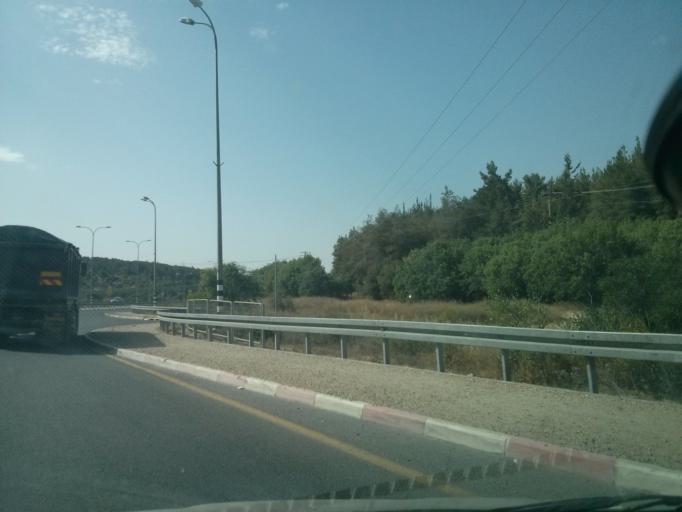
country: IL
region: Jerusalem
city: Bet Shemesh
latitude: 31.7498
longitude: 35.0019
